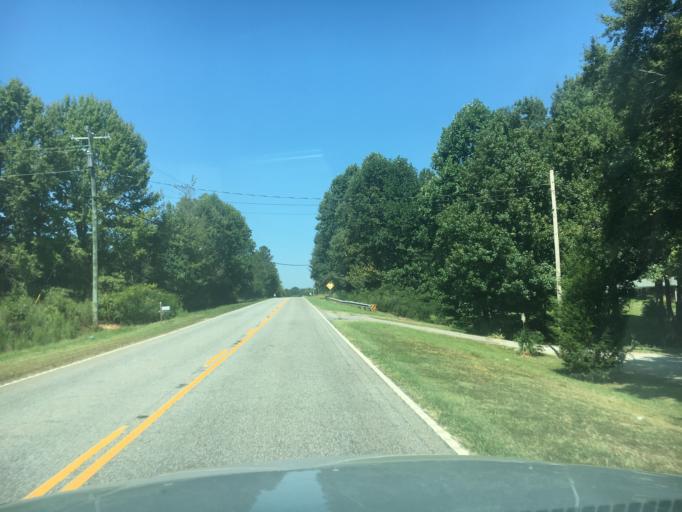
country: US
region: South Carolina
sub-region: Spartanburg County
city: Boiling Springs
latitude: 35.1272
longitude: -82.0347
